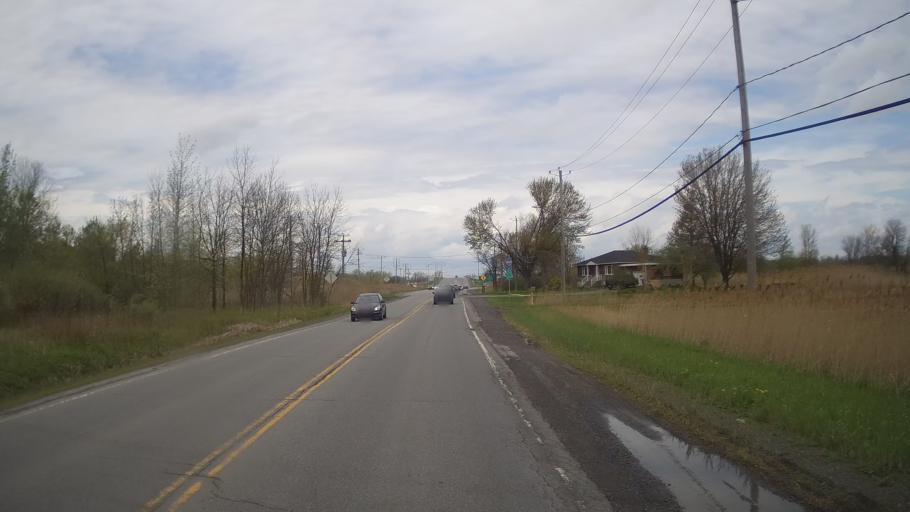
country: CA
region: Quebec
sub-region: Monteregie
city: La Prairie
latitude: 45.4002
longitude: -73.4539
